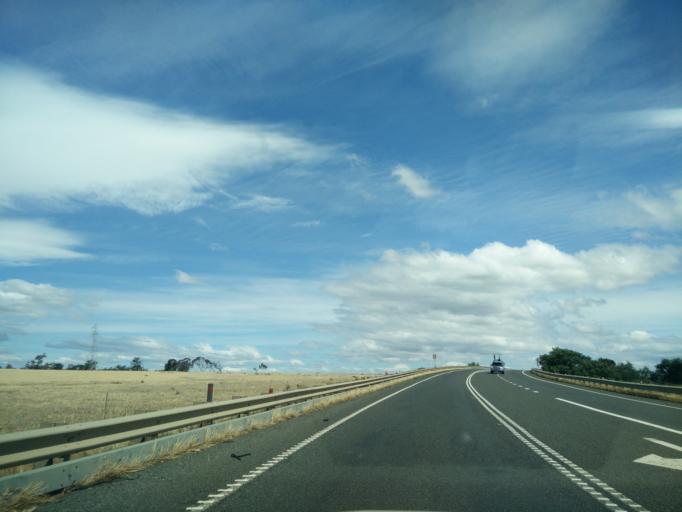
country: AU
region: Tasmania
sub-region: Northern Midlands
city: Evandale
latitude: -41.8366
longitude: 147.4478
